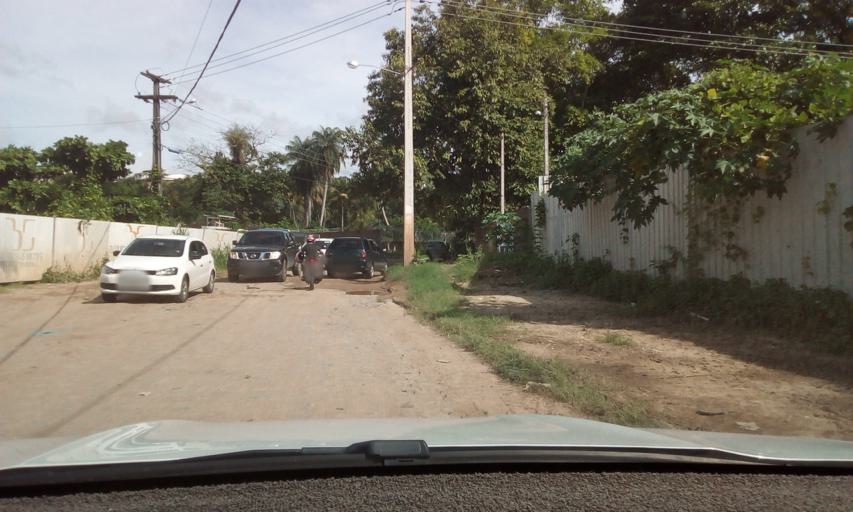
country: BR
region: Paraiba
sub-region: Joao Pessoa
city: Joao Pessoa
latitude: -7.1313
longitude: -34.8869
